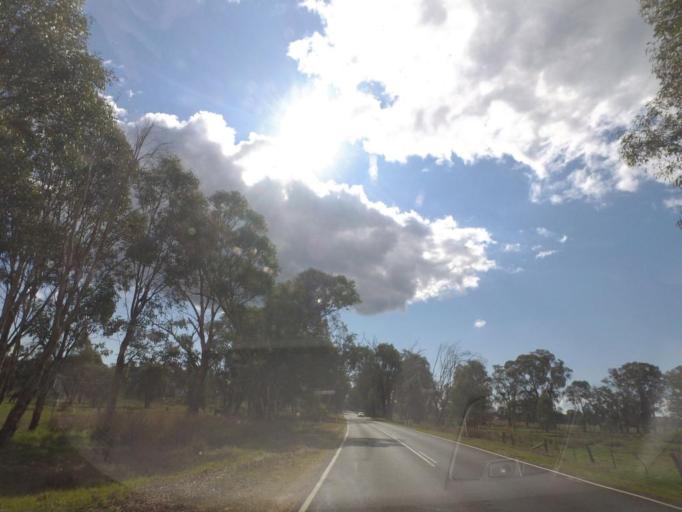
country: AU
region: New South Wales
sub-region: Corowa Shire
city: Howlong
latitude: -36.1684
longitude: 146.6077
